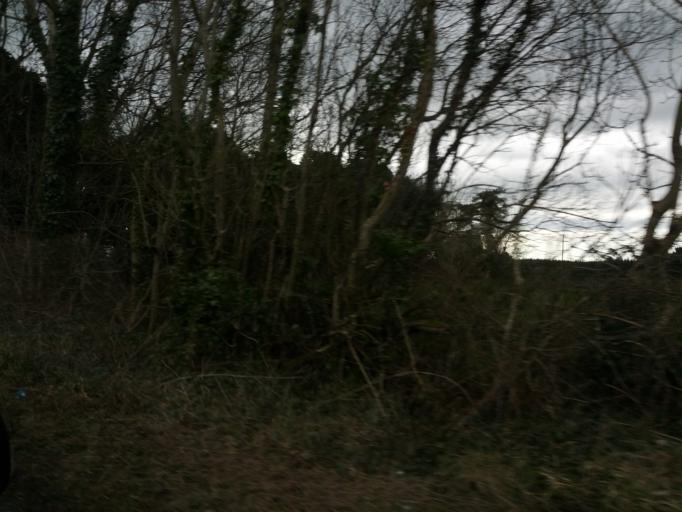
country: IE
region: Connaught
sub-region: County Galway
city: Athenry
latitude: 53.3846
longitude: -8.6244
